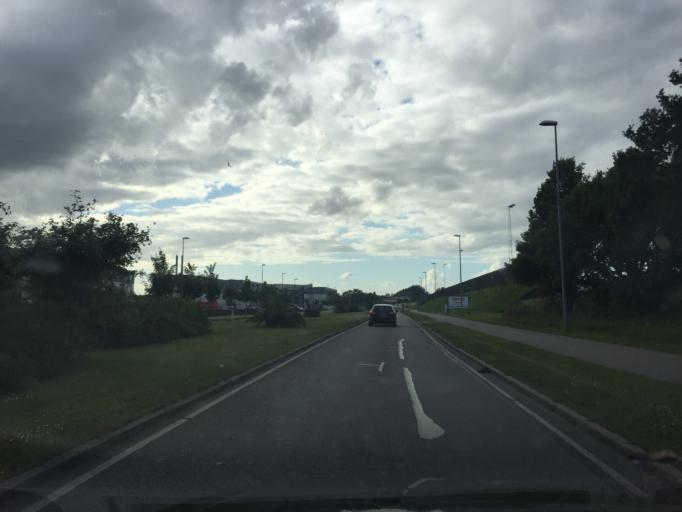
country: DK
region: Capital Region
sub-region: Albertslund Kommune
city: Albertslund
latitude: 55.6534
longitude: 12.3687
